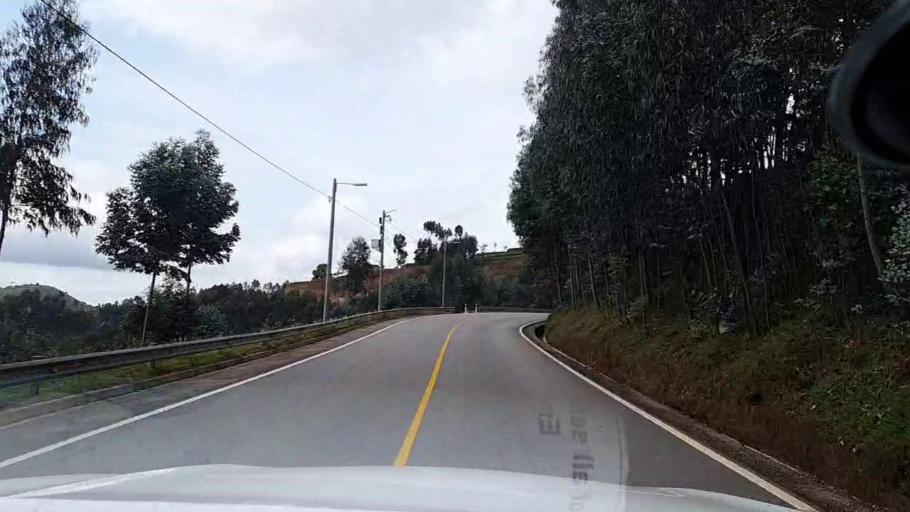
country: RW
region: Southern Province
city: Nzega
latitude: -2.5174
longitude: 29.4602
